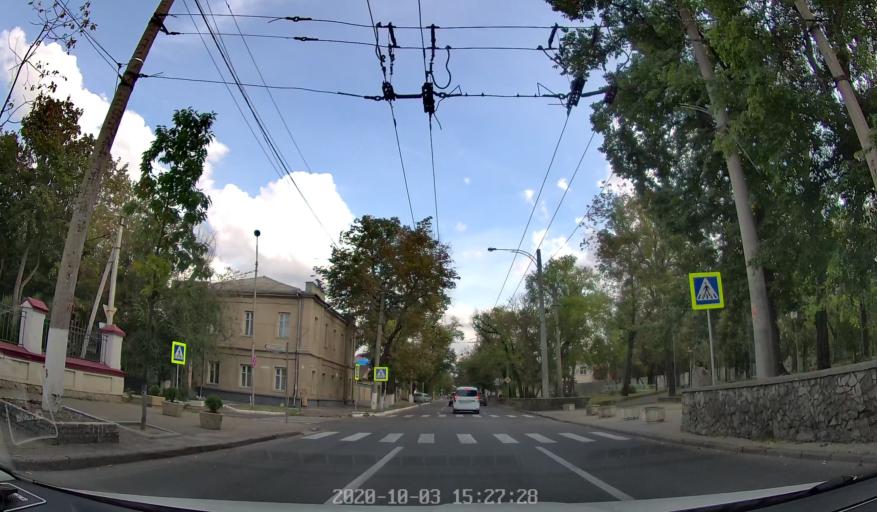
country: MD
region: Chisinau
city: Chisinau
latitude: 47.0245
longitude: 28.8177
